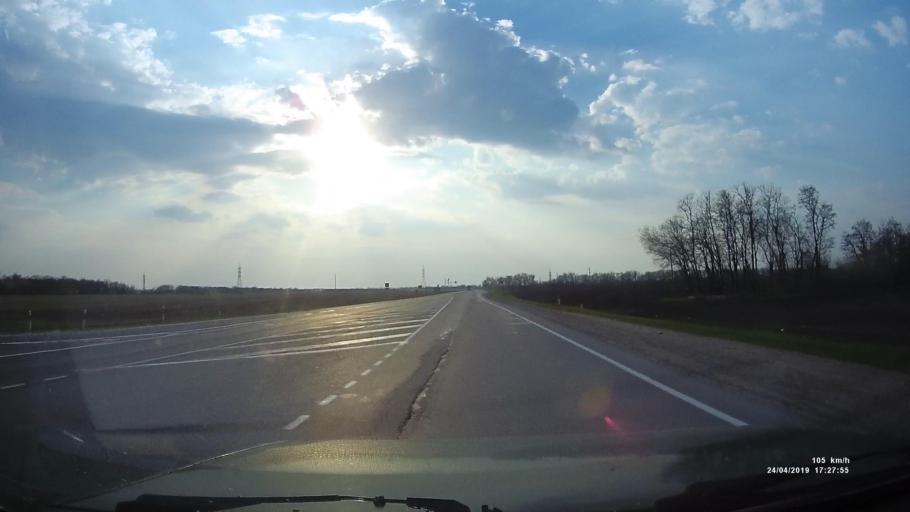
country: RU
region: Rostov
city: Gigant
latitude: 46.5300
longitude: 41.1894
